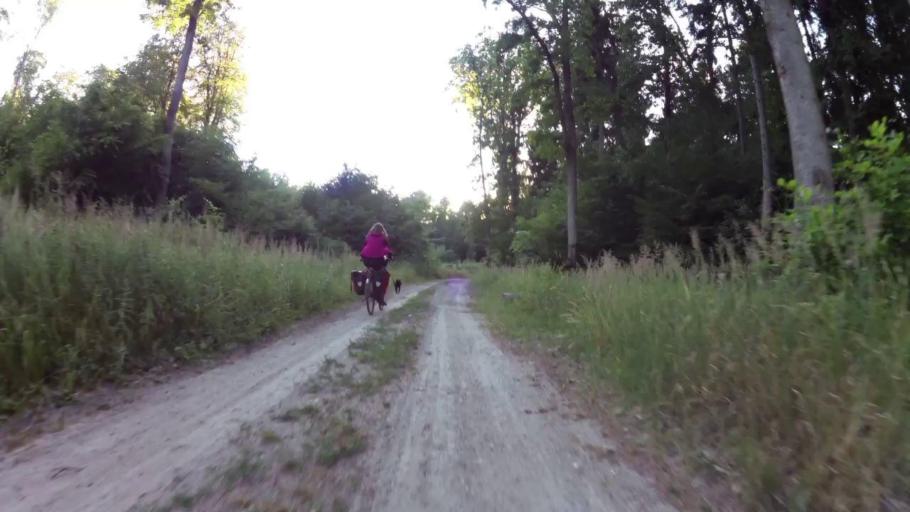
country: PL
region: West Pomeranian Voivodeship
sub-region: Powiat lobeski
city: Lobez
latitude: 53.7515
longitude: 15.6332
